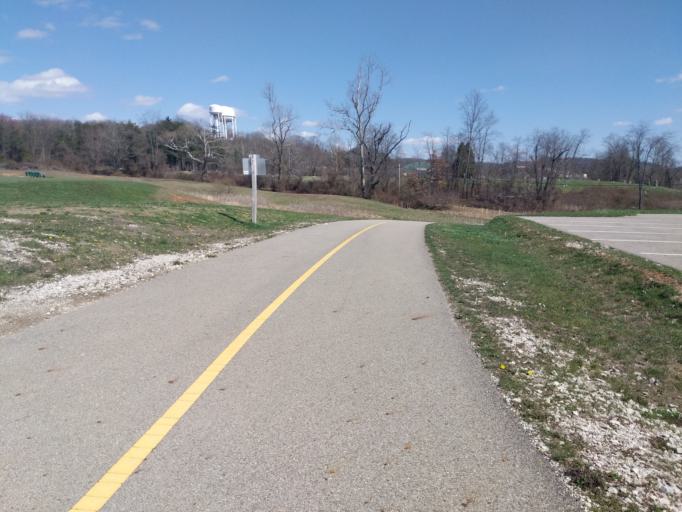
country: US
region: Ohio
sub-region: Athens County
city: The Plains
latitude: 39.3692
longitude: -82.1262
